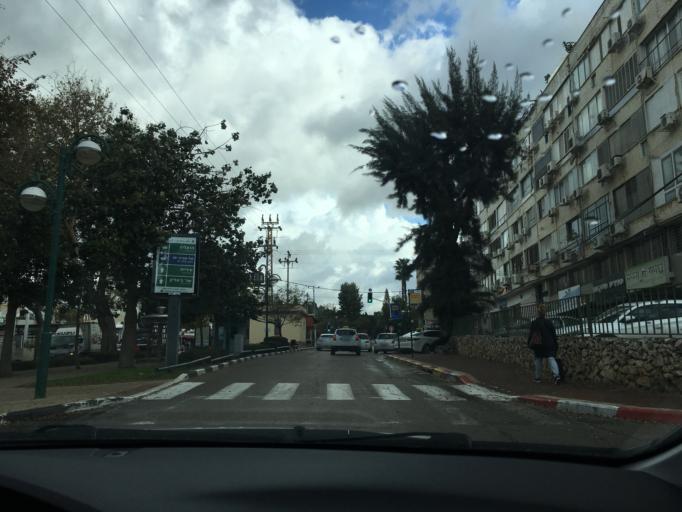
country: IL
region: Tel Aviv
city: Ramat HaSharon
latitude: 32.1461
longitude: 34.8376
